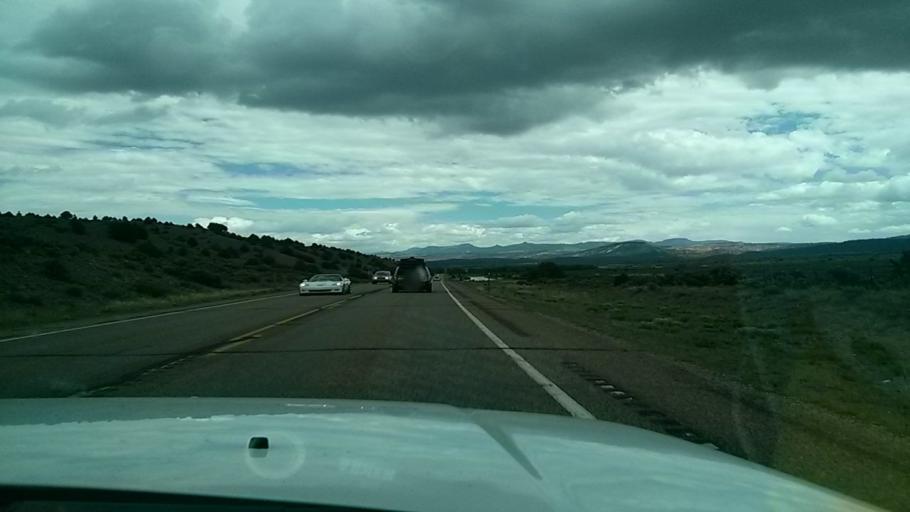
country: US
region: Utah
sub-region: Garfield County
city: Panguitch
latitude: 37.6994
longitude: -112.3991
